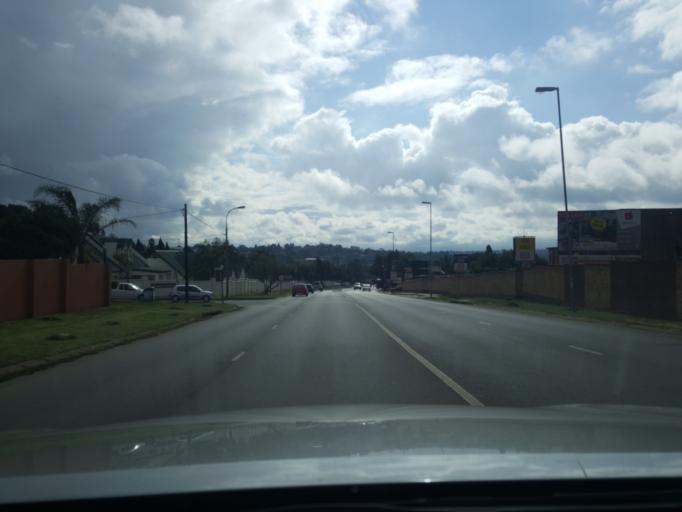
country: ZA
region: Gauteng
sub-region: City of Johannesburg Metropolitan Municipality
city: Roodepoort
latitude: -26.1642
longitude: 27.9493
